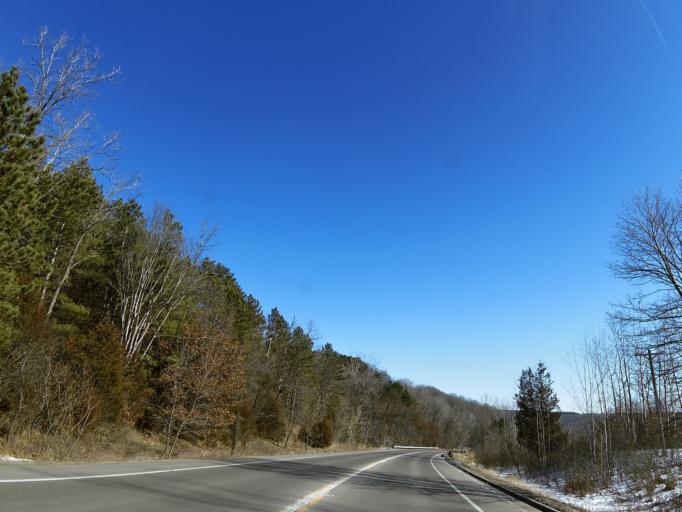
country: US
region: Minnesota
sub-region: Washington County
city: Stillwater
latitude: 45.0774
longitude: -92.8161
